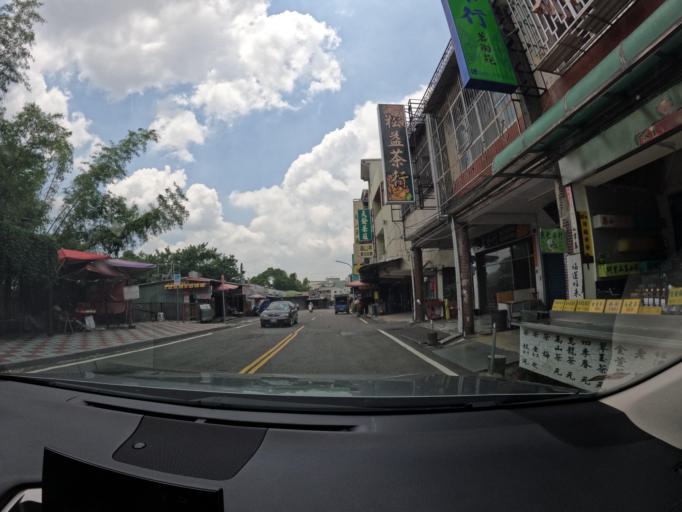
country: TW
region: Taiwan
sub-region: Nantou
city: Nantou
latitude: 23.8332
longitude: 120.6344
